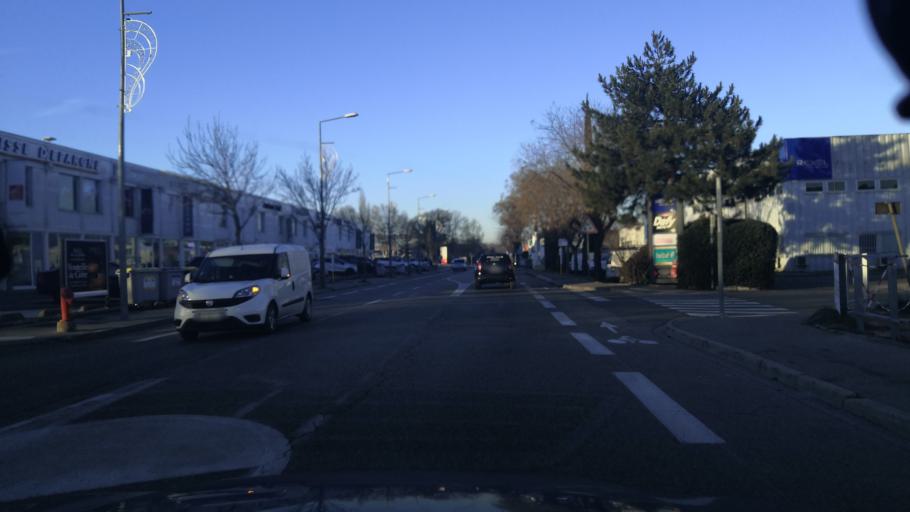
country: FR
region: Provence-Alpes-Cote d'Azur
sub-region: Departement des Bouches-du-Rhone
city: Aix-en-Provence
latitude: 43.5075
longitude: 5.4014
